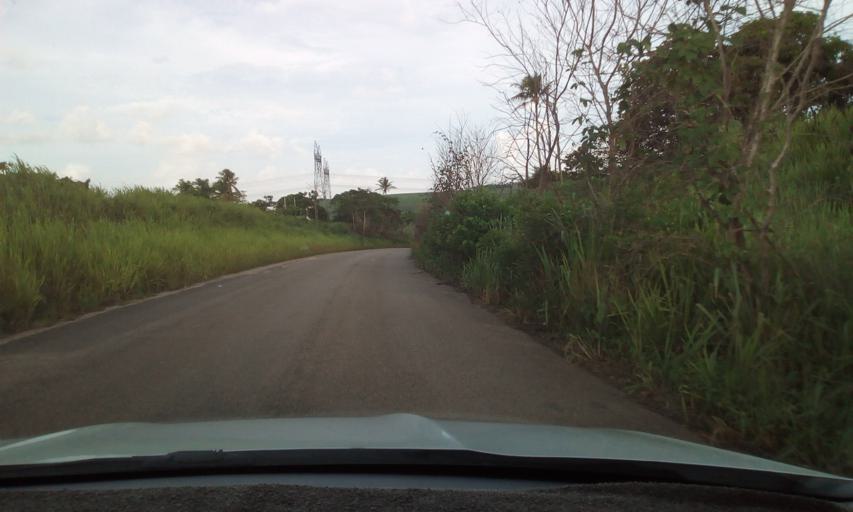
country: BR
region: Pernambuco
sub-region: Gloria Do Goita
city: Gloria do Goita
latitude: -7.9883
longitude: -35.2386
